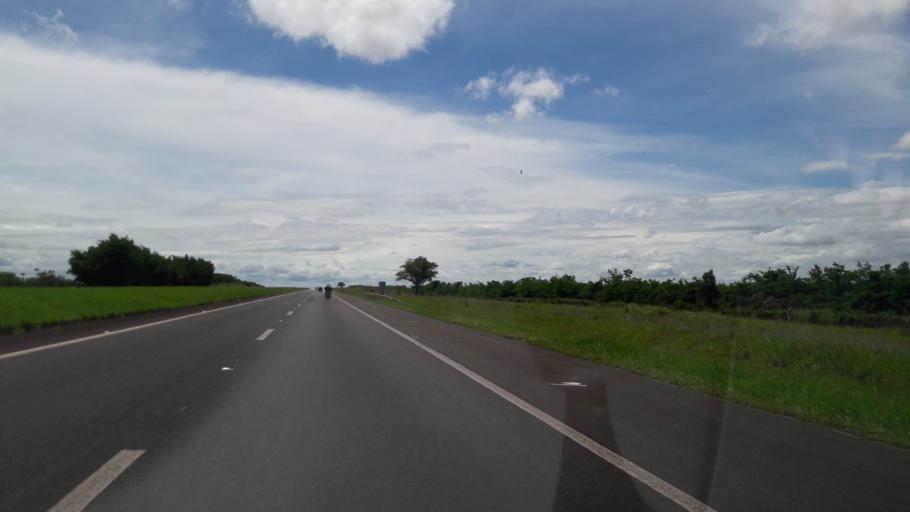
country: BR
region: Sao Paulo
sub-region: Avare
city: Avare
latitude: -22.9481
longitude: -48.8871
